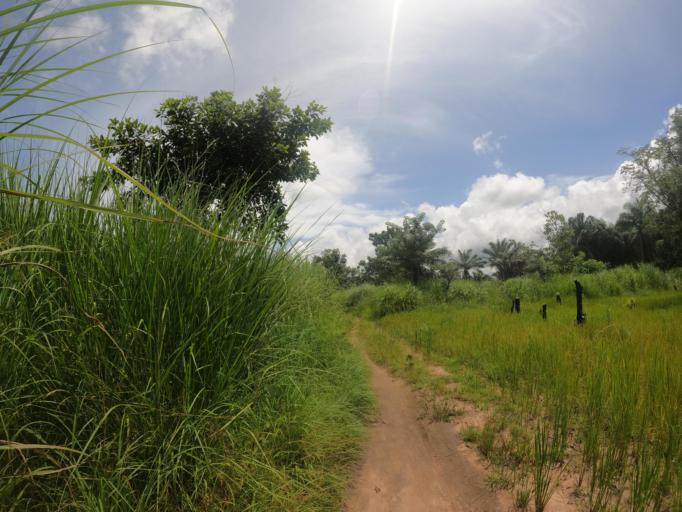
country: SL
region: Northern Province
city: Makeni
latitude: 9.1259
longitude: -12.2609
